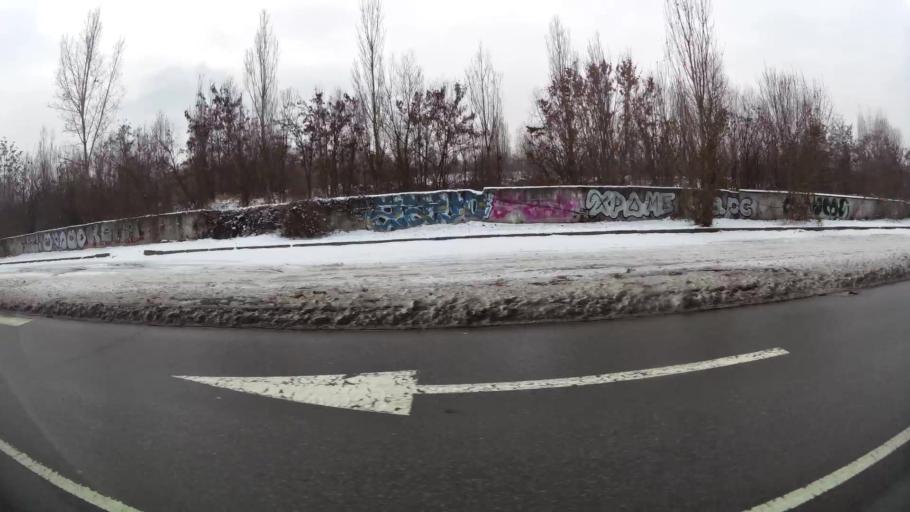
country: BG
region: Sofia-Capital
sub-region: Stolichna Obshtina
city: Sofia
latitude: 42.7154
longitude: 23.3241
